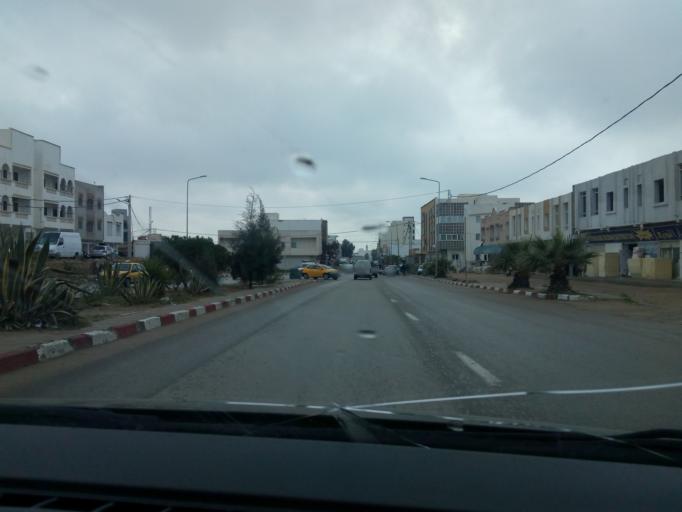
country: TN
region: Madanin
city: Medenine
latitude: 33.3562
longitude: 10.4761
